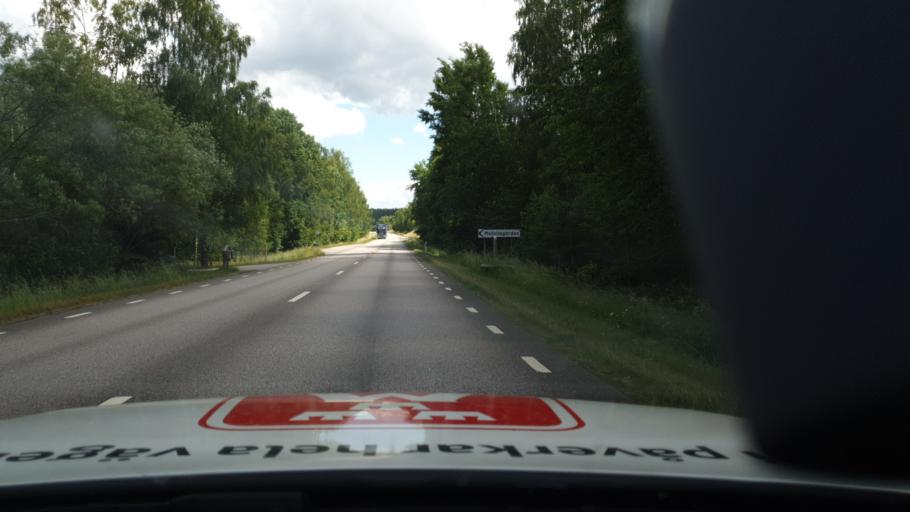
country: SE
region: Vaestra Goetaland
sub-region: Tibro Kommun
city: Tibro
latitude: 58.3419
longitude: 14.1846
